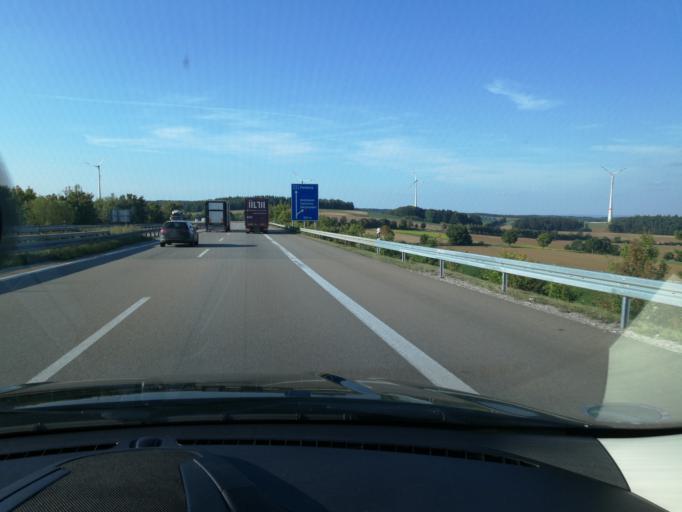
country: DE
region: Bavaria
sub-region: Upper Palatinate
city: Brunn
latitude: 49.1384
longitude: 11.8627
